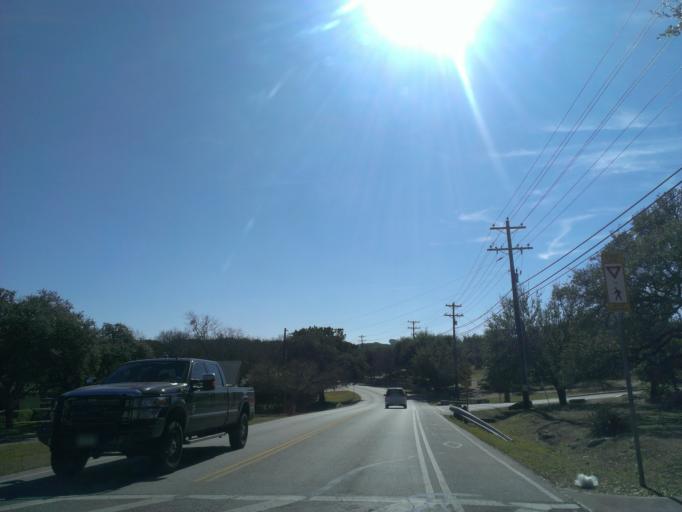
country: US
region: Texas
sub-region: Travis County
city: Lakeway
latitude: 30.3653
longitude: -97.9807
